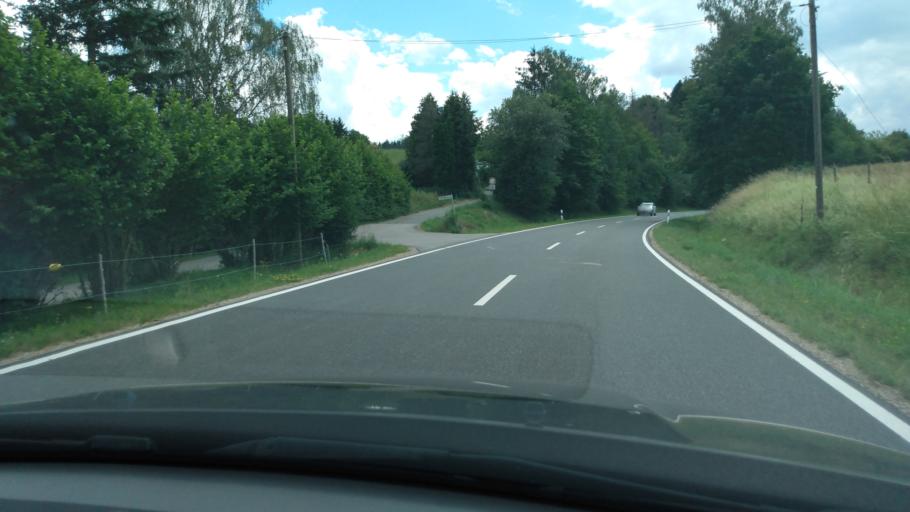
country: DE
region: Rheinland-Pfalz
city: Udersdorf
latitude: 50.1455
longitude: 6.7998
